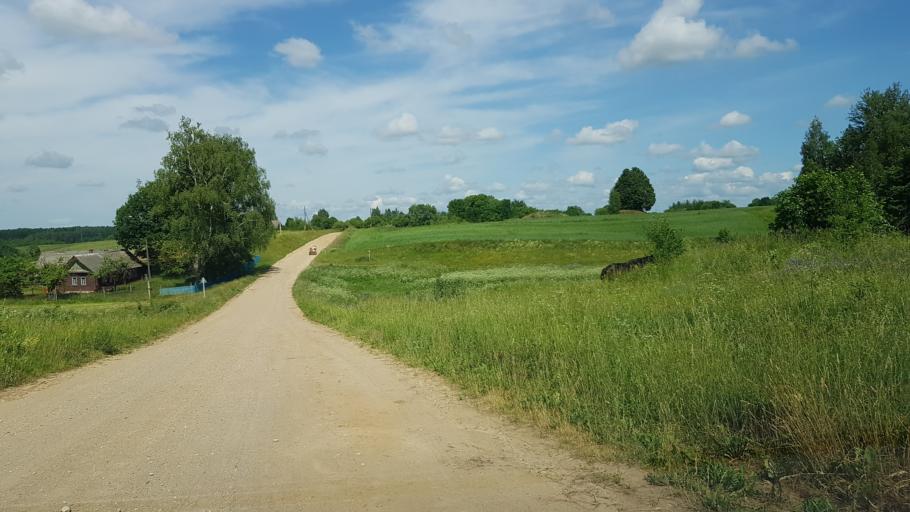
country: BY
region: Vitebsk
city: Dubrowna
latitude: 54.4851
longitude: 30.7991
